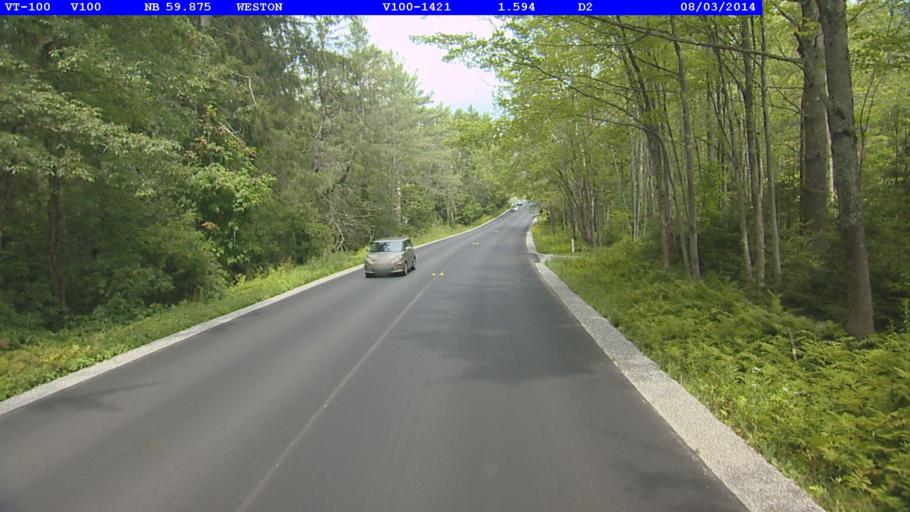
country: US
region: Vermont
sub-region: Windsor County
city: Chester
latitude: 43.2694
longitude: -72.7889
